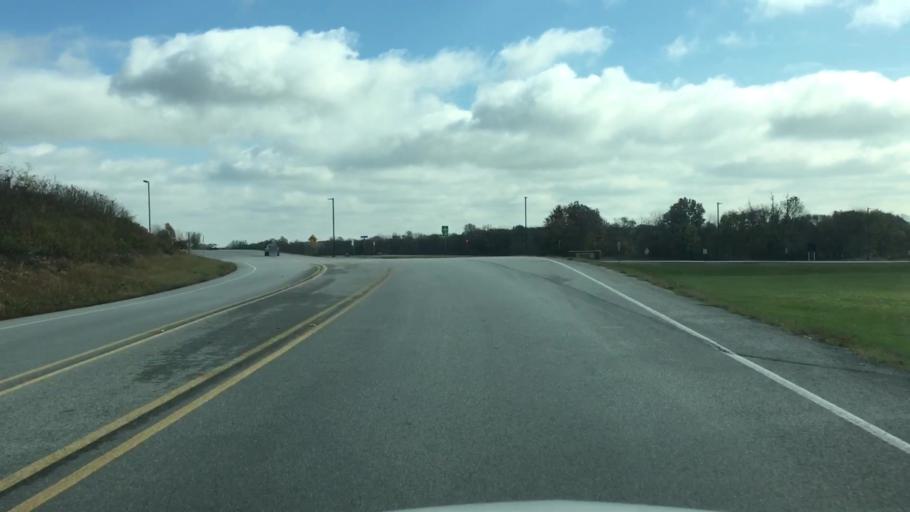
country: US
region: Arkansas
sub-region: Benton County
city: Centerton
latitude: 36.3008
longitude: -94.3081
